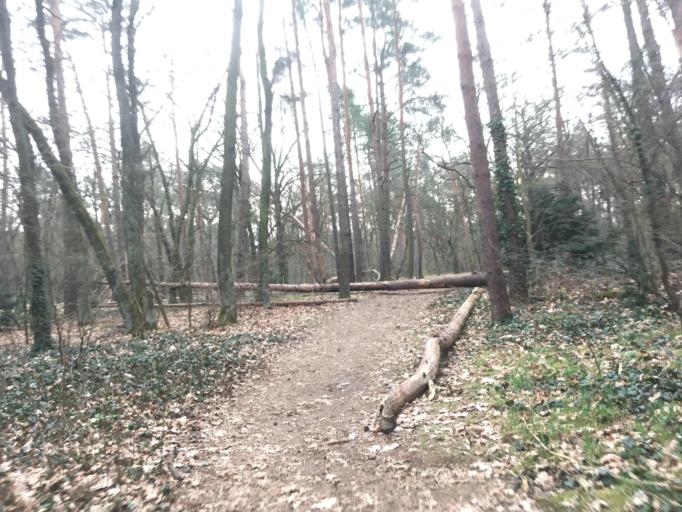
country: DE
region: Berlin
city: Baumschulenweg
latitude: 52.4569
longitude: 13.4893
